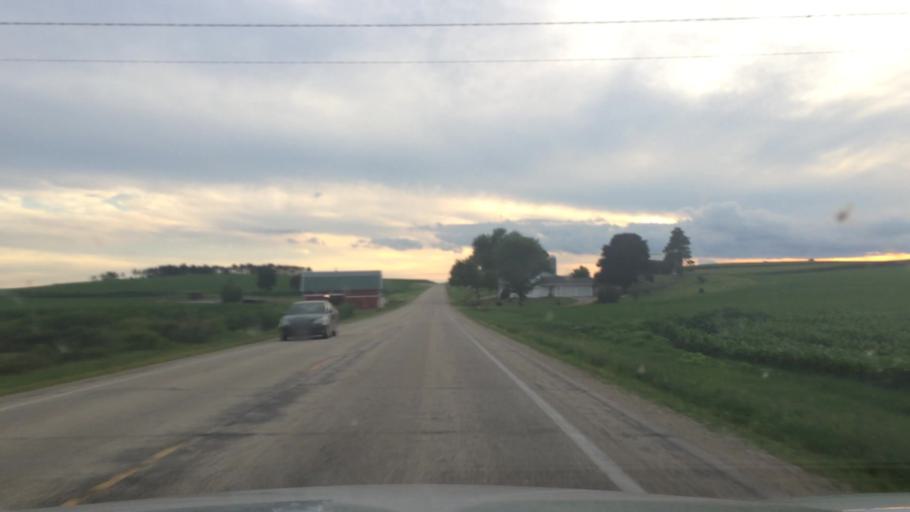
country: US
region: Wisconsin
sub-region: Columbia County
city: Lodi
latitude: 43.2357
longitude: -89.5302
